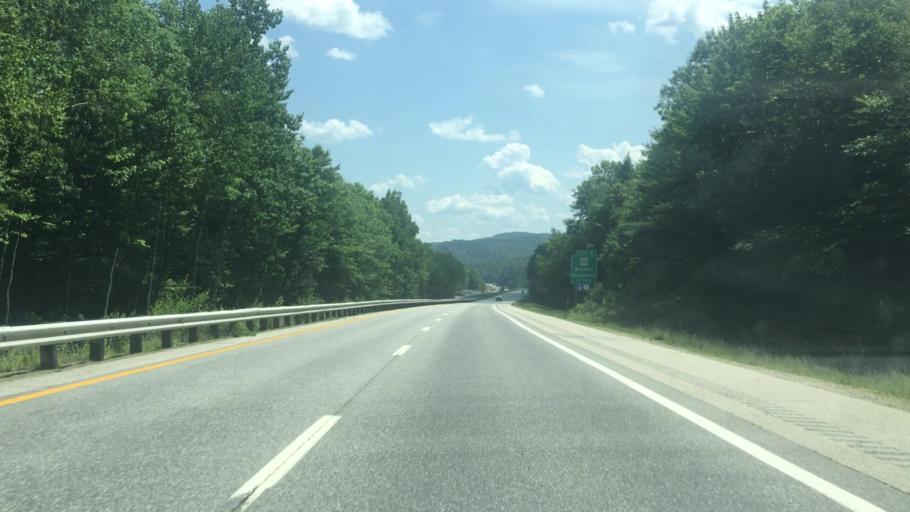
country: US
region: New Hampshire
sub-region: Merrimack County
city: Sutton
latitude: 43.2997
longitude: -71.8409
